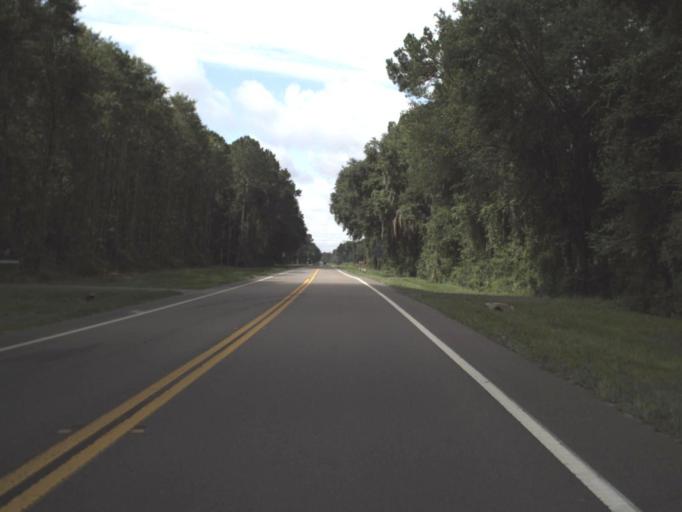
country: US
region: Florida
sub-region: Columbia County
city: Five Points
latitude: 30.3207
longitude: -82.6301
